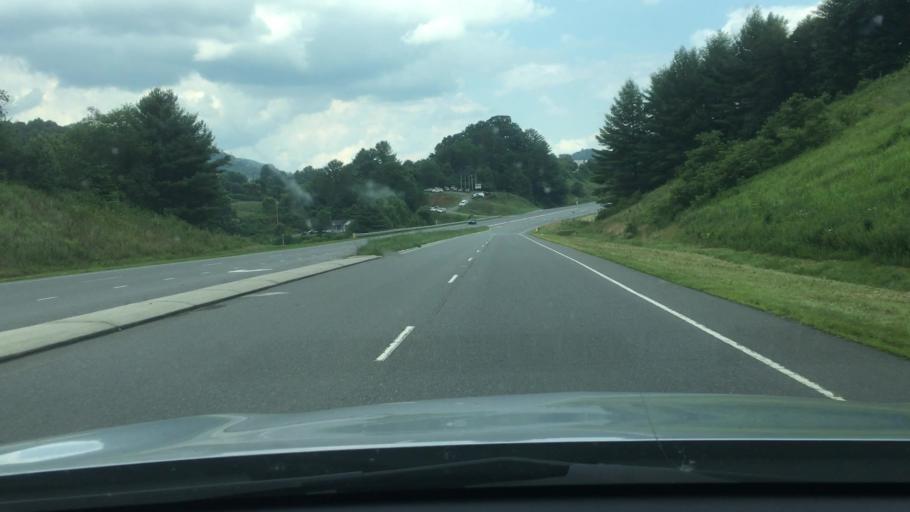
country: US
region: North Carolina
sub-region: Yancey County
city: Burnsville
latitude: 35.9109
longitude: -82.3707
